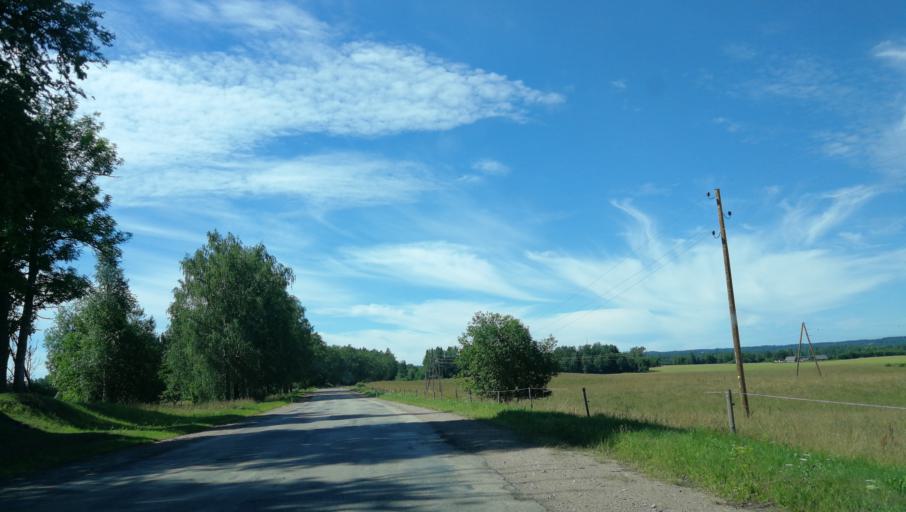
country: LV
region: Cesvaine
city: Cesvaine
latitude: 57.0048
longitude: 26.4026
